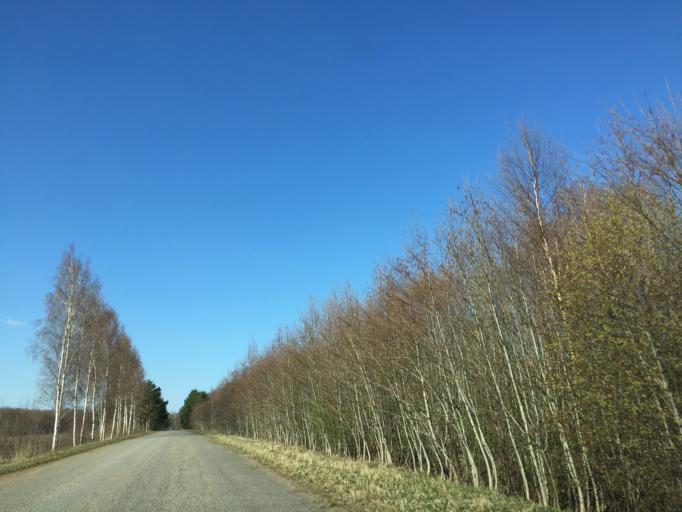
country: EE
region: Valgamaa
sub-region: Torva linn
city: Torva
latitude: 58.2481
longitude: 25.9498
